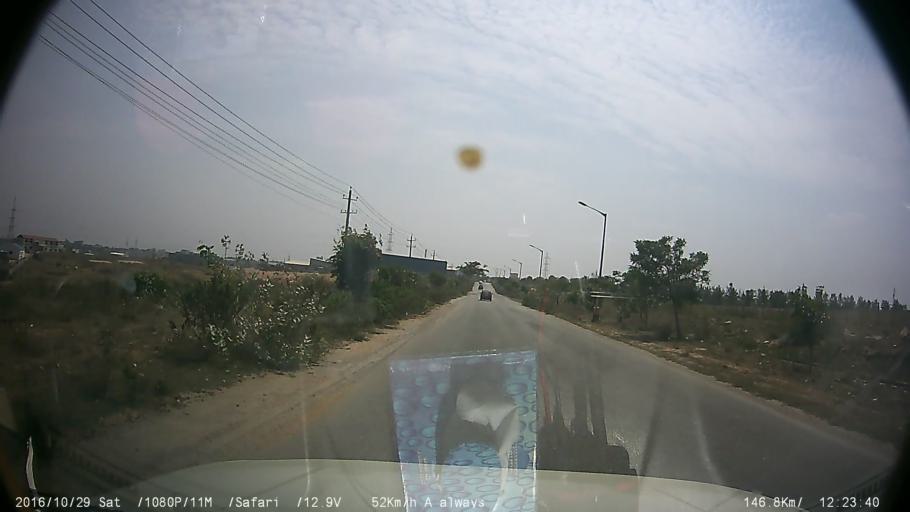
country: IN
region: Karnataka
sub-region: Mysore
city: Mysore
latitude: 12.3589
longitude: 76.5627
